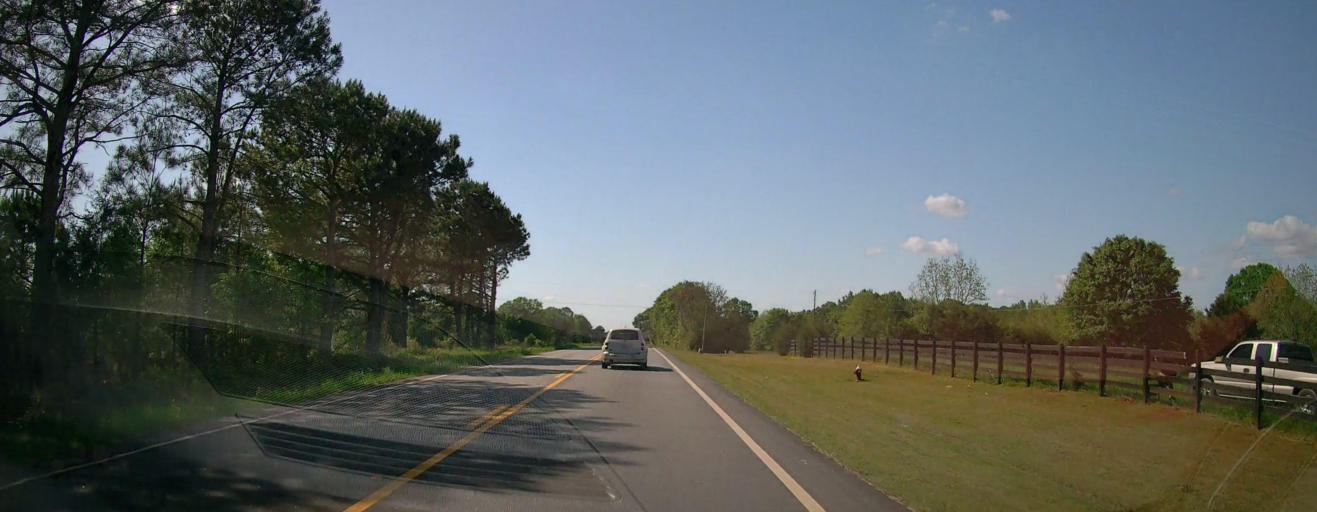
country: US
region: Georgia
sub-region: Morgan County
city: Madison
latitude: 33.6061
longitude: -83.4289
